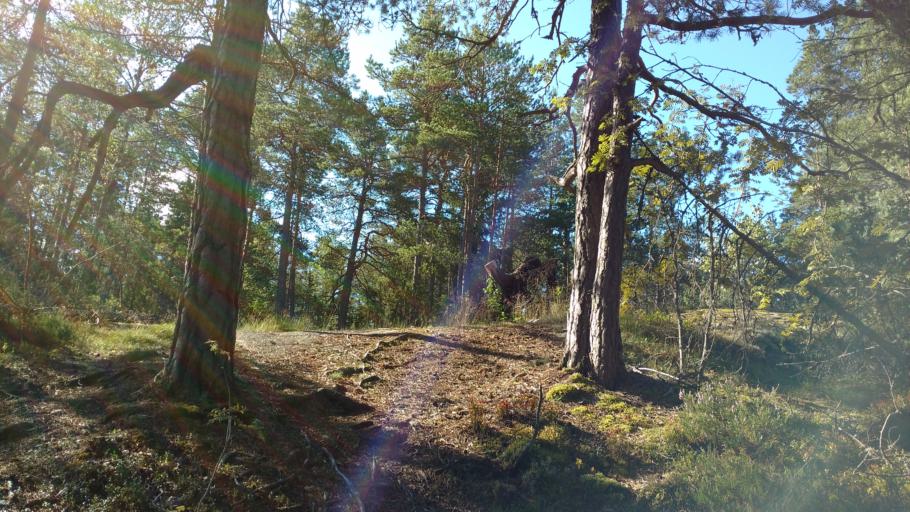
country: FI
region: Varsinais-Suomi
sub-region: Salo
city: Salo
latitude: 60.3823
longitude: 23.1698
